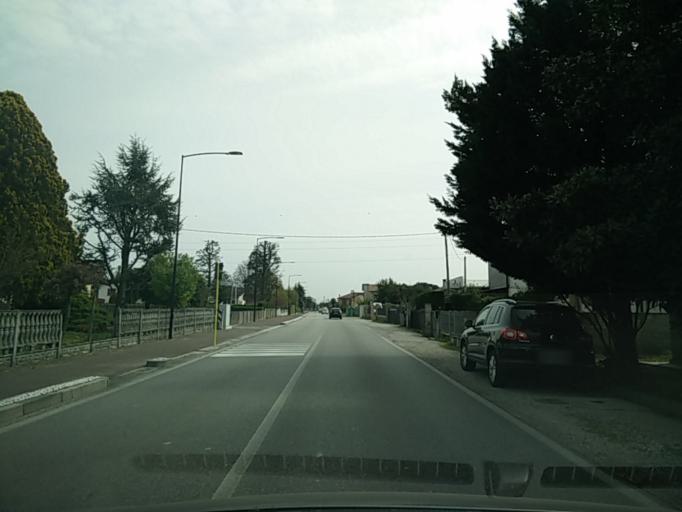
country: IT
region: Veneto
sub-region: Provincia di Venezia
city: Scaltenigo
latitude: 45.4697
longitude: 12.0937
